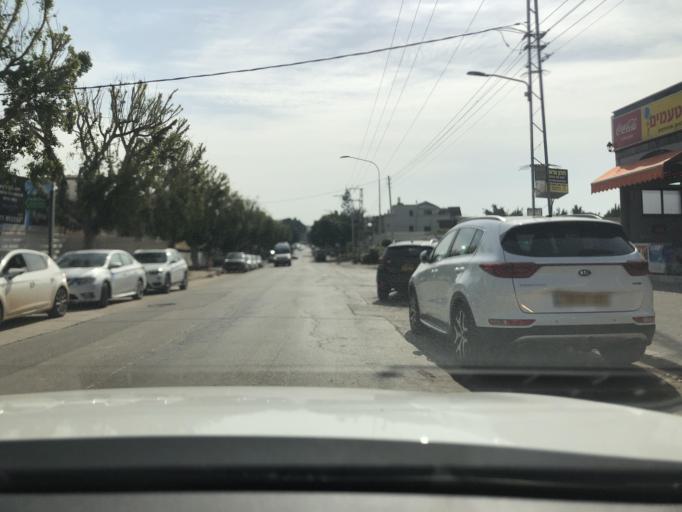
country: IL
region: Central District
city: Rosh Ha'Ayin
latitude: 32.0934
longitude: 34.9461
